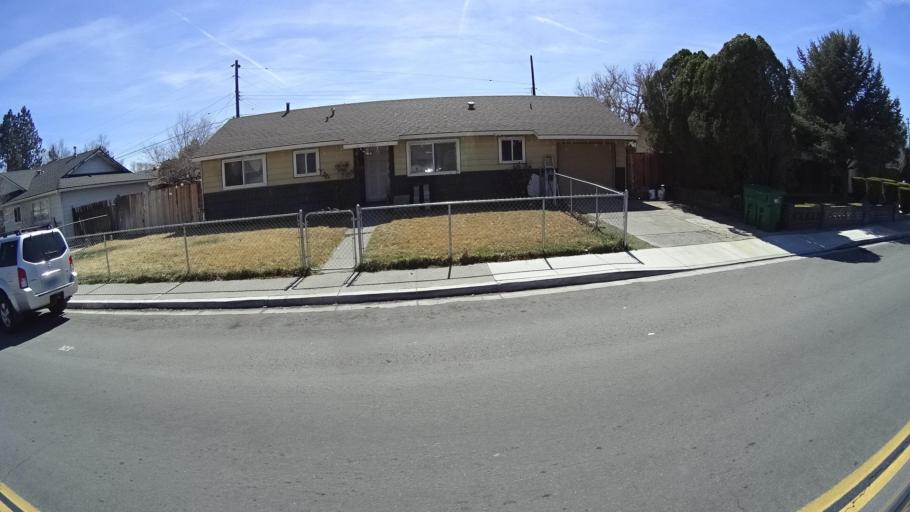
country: US
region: Nevada
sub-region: Washoe County
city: Sparks
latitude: 39.5473
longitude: -119.7688
